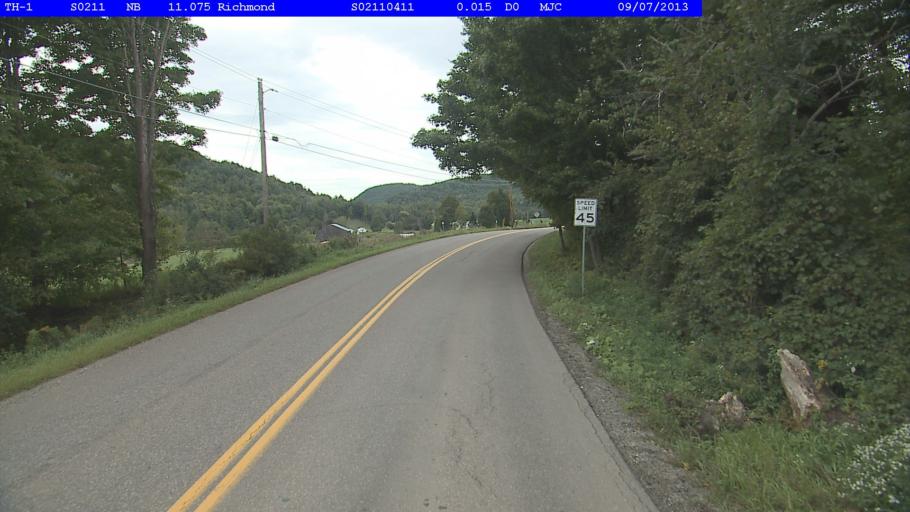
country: US
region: Vermont
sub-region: Chittenden County
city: Williston
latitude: 44.3536
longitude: -72.9927
